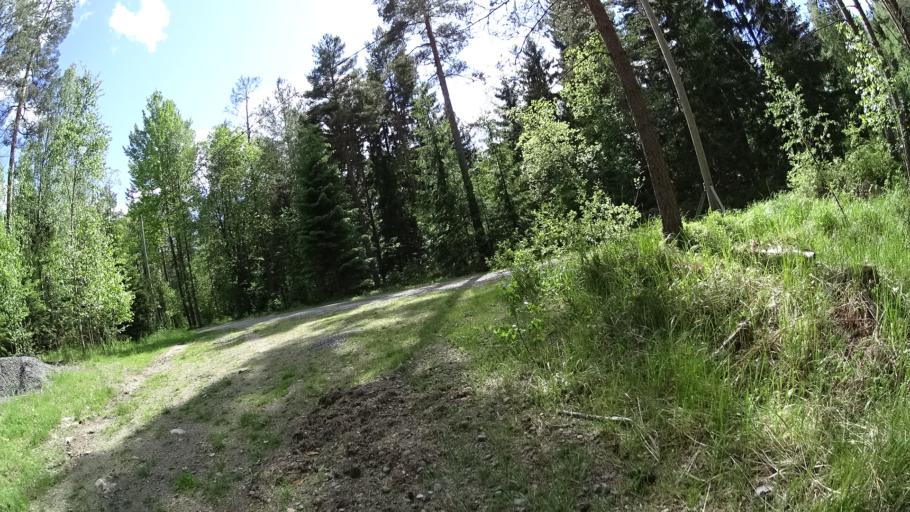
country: FI
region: Uusimaa
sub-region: Raaseporin
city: Pohja
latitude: 60.1825
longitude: 23.5849
